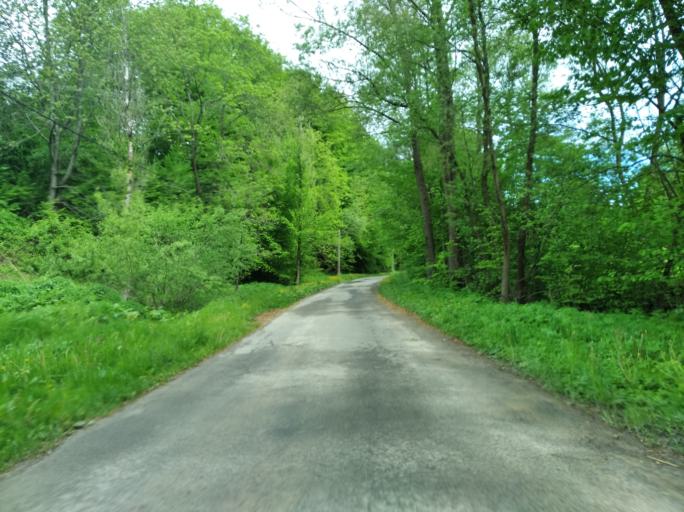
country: PL
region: Subcarpathian Voivodeship
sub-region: Powiat strzyzowski
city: Strzyzow
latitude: 49.9234
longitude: 21.7539
